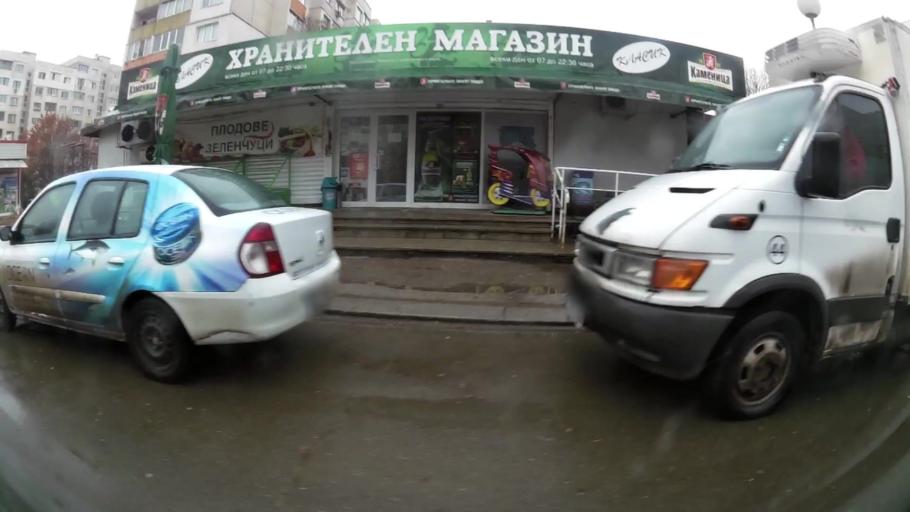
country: BG
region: Sofia-Capital
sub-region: Stolichna Obshtina
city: Sofia
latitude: 42.6508
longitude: 23.4021
